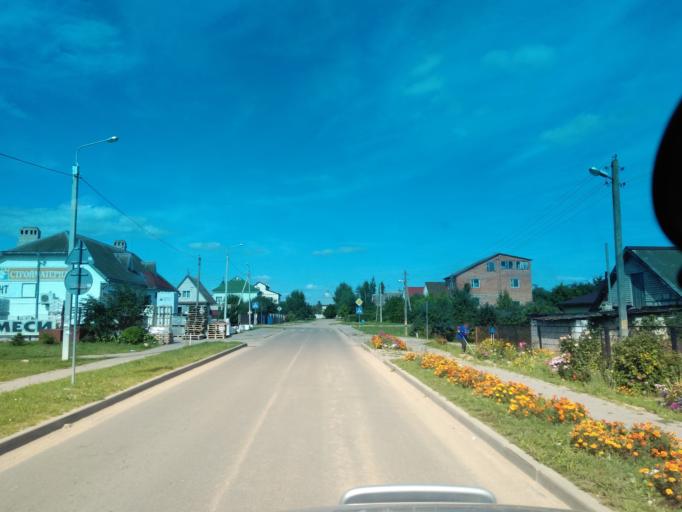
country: BY
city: Fanipol
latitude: 53.7523
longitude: 27.3363
